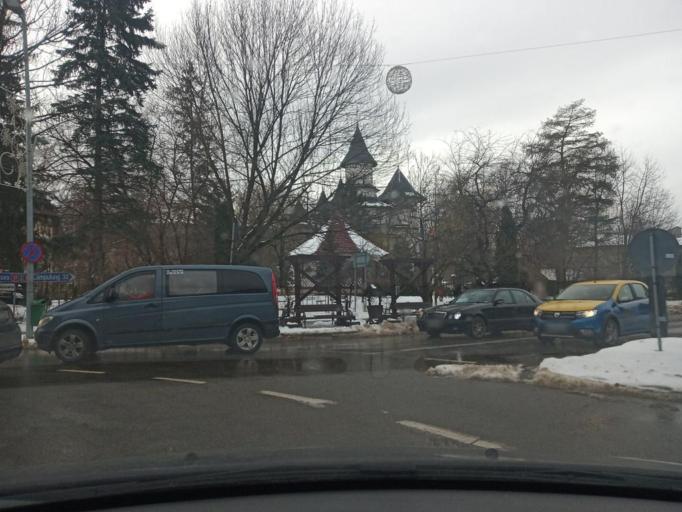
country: RO
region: Suceava
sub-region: Oras Gura Humorului
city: Gura Humorului
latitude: 47.5550
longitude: 25.8903
